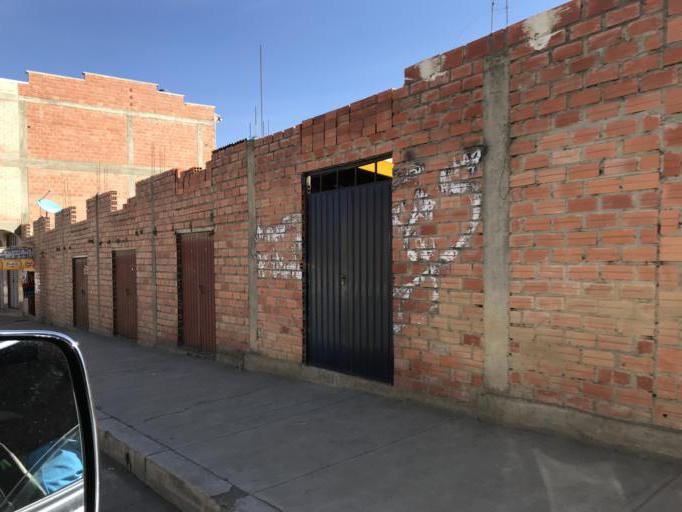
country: BO
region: La Paz
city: La Paz
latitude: -16.4868
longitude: -68.1831
